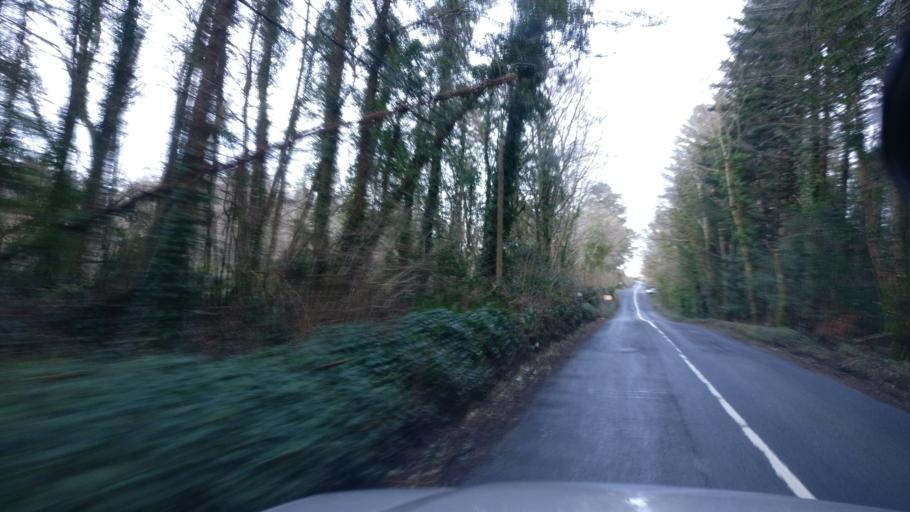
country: IE
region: Connaught
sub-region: County Galway
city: Oughterard
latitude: 53.5326
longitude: -9.3213
